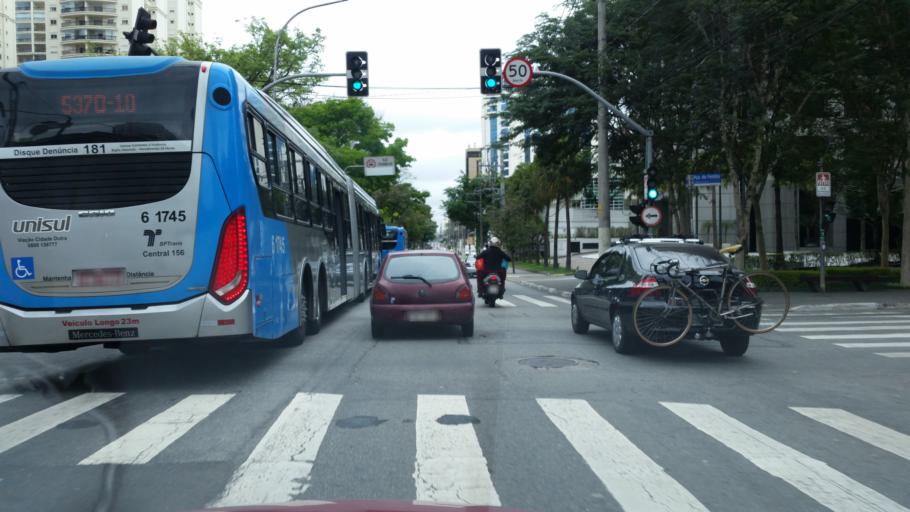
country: BR
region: Sao Paulo
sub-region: Sao Paulo
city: Sao Paulo
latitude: -23.6039
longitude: -46.6626
